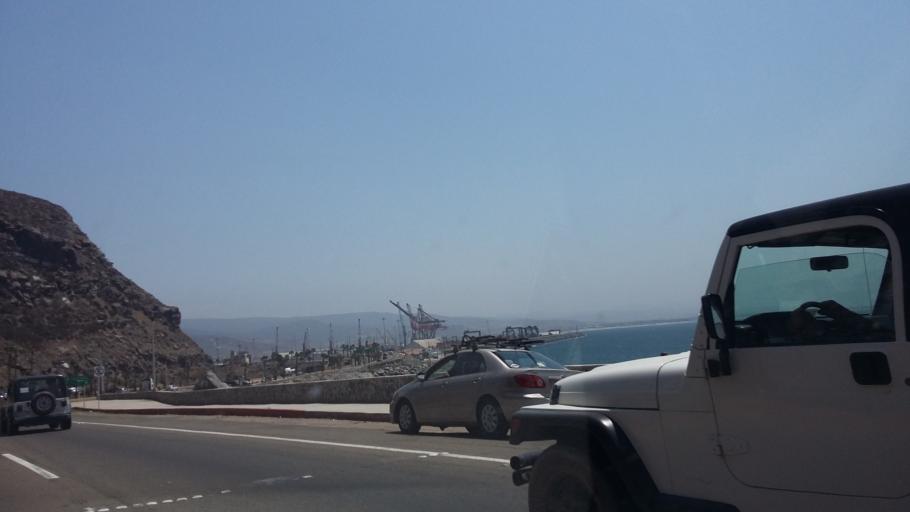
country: MX
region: Baja California
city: Ensenada
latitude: 31.8609
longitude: -116.6410
